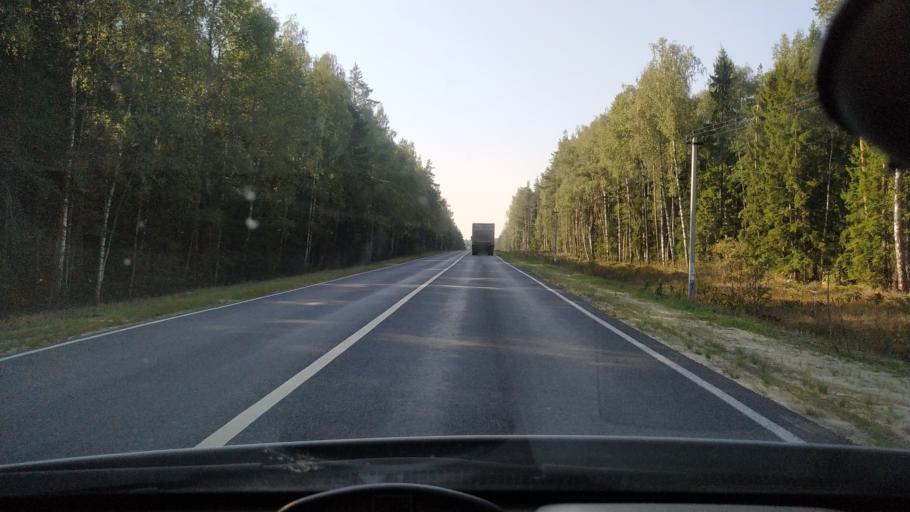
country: RU
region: Moskovskaya
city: Tugolesskiy Bor
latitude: 55.4972
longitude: 39.7141
